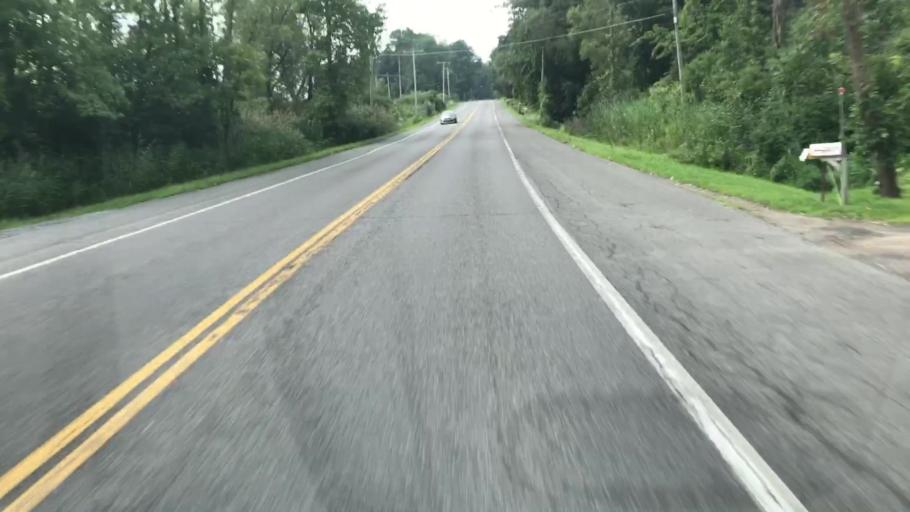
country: US
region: New York
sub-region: Onondaga County
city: Liverpool
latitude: 43.1688
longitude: -76.1963
